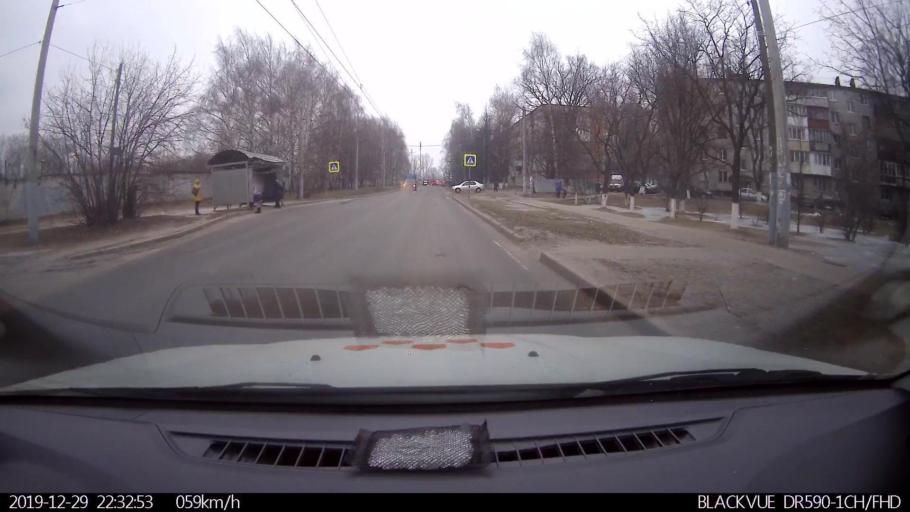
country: RU
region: Nizjnij Novgorod
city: Gorbatovka
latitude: 56.2597
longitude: 43.8658
